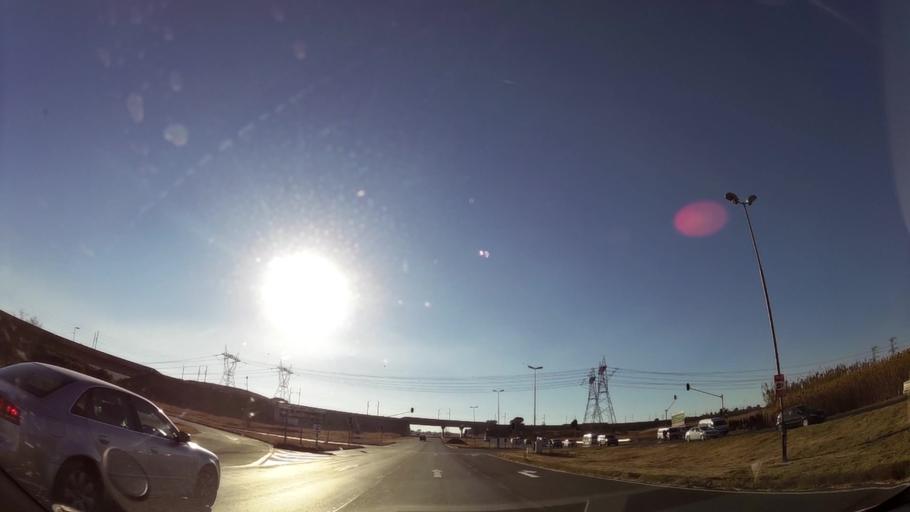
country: ZA
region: Gauteng
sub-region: City of Johannesburg Metropolitan Municipality
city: Modderfontein
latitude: -26.1036
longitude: 28.1762
